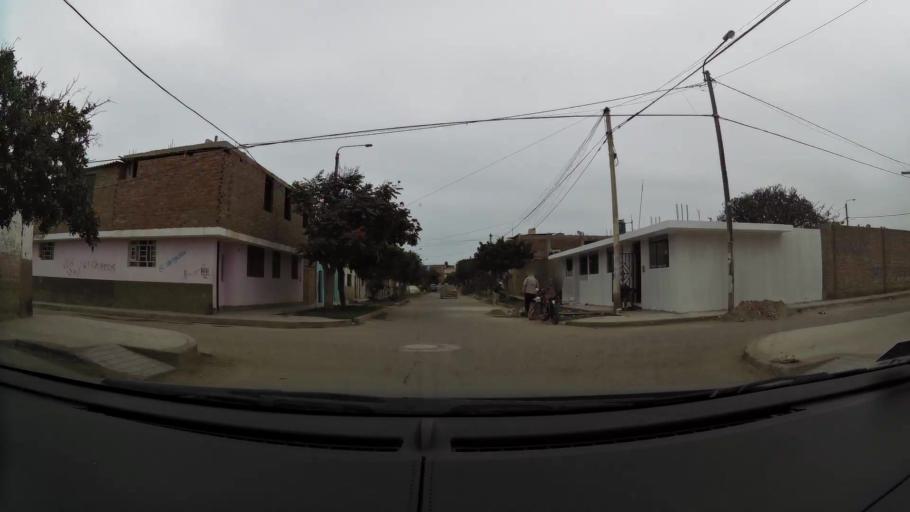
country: PE
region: La Libertad
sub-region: Provincia de Trujillo
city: Buenos Aires
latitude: -8.1431
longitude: -79.0514
